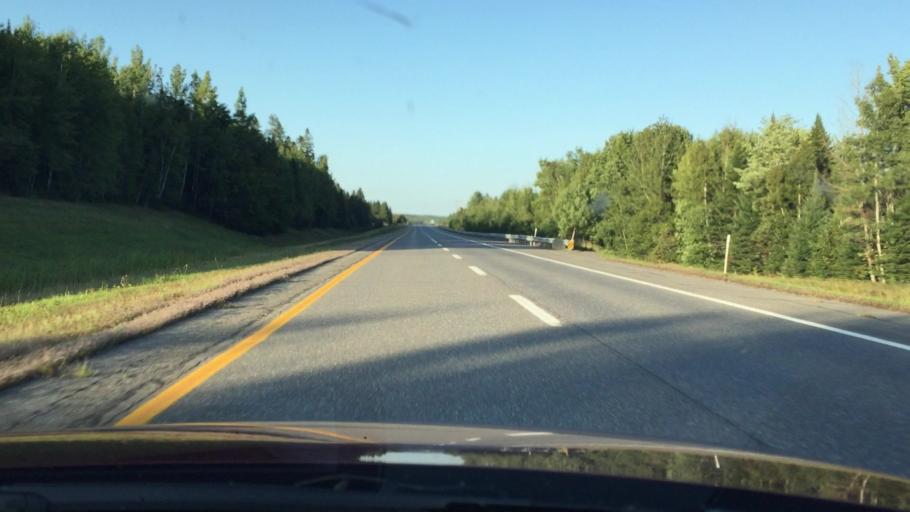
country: US
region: Maine
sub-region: Aroostook County
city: Hodgdon
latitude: 46.1322
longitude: -68.0892
